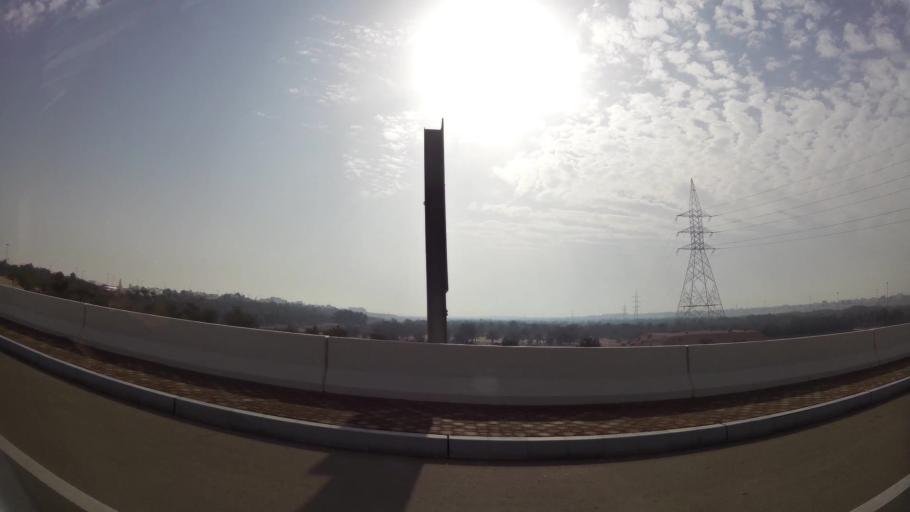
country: AE
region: Abu Dhabi
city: Abu Dhabi
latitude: 24.2547
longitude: 54.7099
